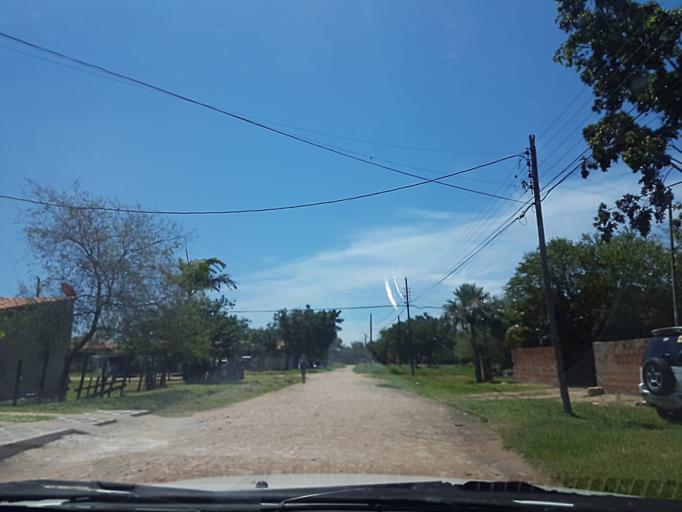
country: PY
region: Central
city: Limpio
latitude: -25.1842
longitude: -57.4878
